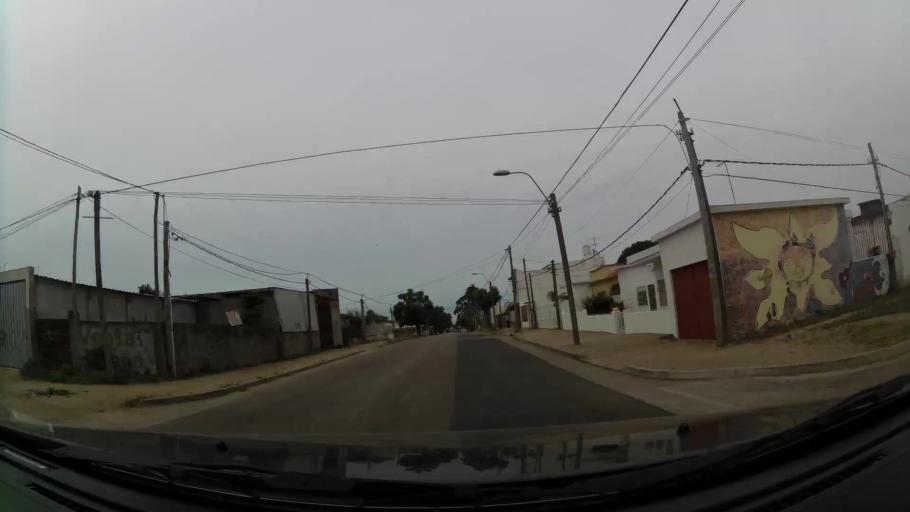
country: UY
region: Canelones
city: La Paz
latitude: -34.7592
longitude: -56.2279
